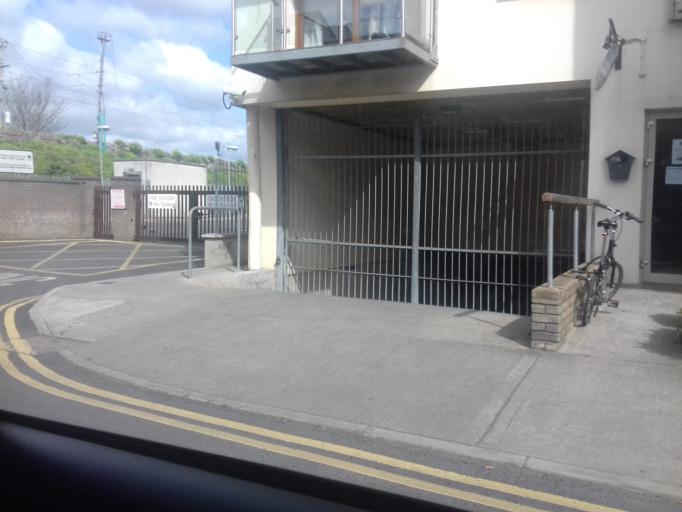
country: IE
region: Leinster
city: Malahide
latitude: 53.4522
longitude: -6.1557
